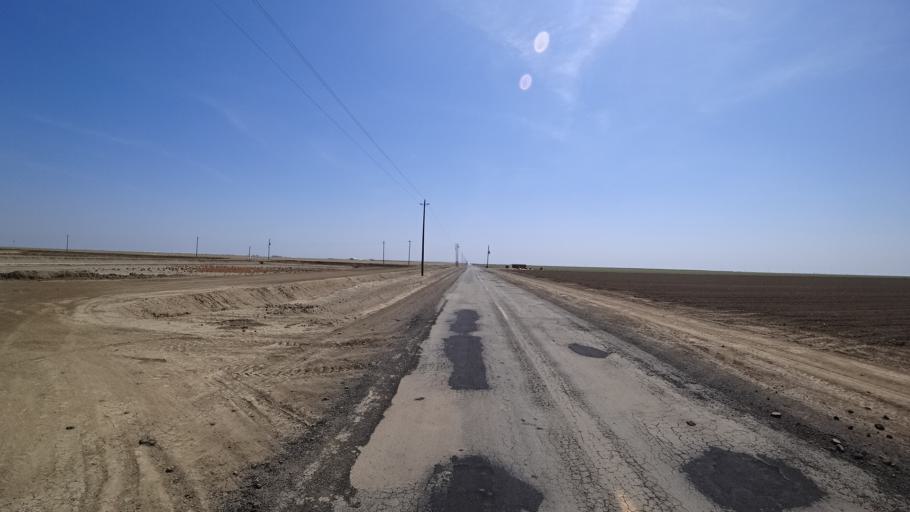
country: US
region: California
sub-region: Kings County
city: Kettleman City
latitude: 36.0942
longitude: -119.9518
